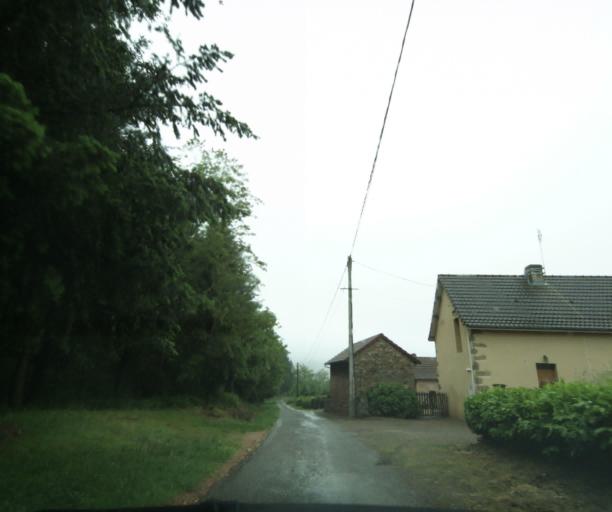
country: FR
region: Bourgogne
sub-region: Departement de Saone-et-Loire
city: Charolles
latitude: 46.3869
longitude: 4.3725
